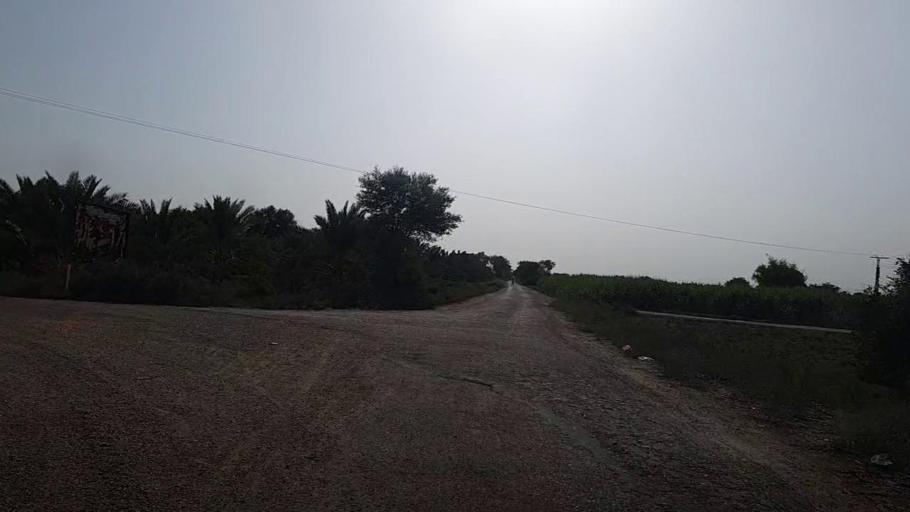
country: PK
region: Sindh
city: Pad Idan
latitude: 26.8532
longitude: 68.3249
